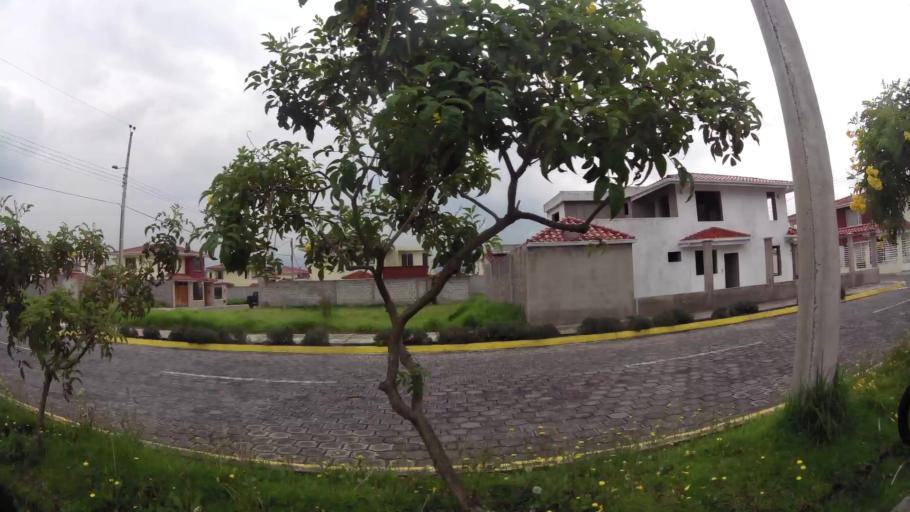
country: EC
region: Pichincha
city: Sangolqui
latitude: -0.3339
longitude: -78.4647
